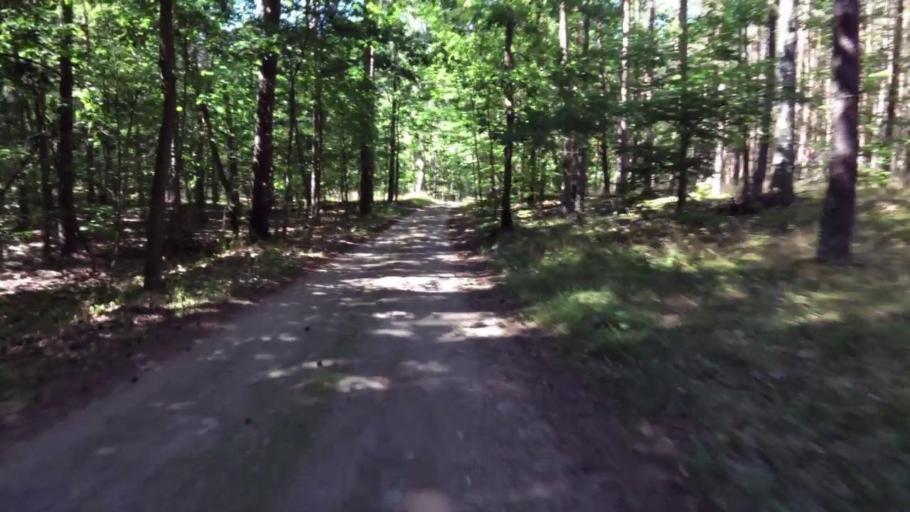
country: PL
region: West Pomeranian Voivodeship
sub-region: Powiat szczecinecki
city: Borne Sulinowo
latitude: 53.6660
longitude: 16.5608
